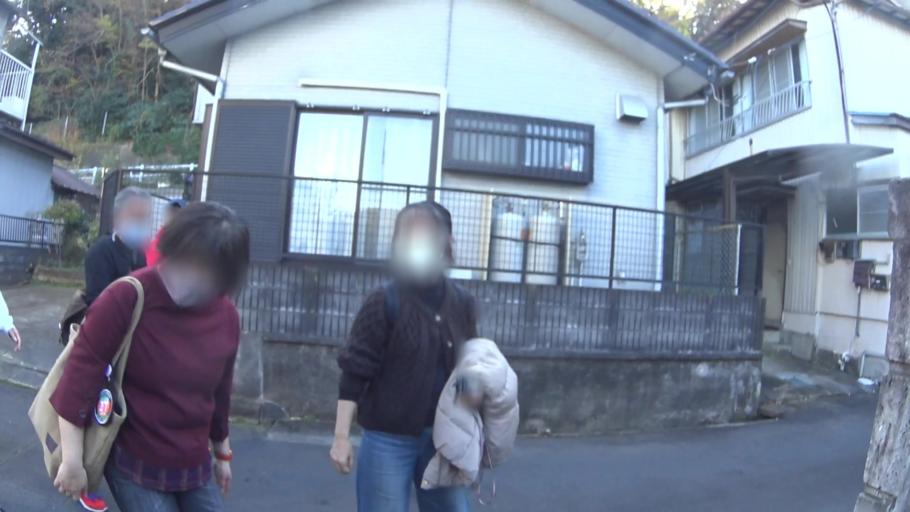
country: JP
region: Ibaraki
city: Mito-shi
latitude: 36.3820
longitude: 140.4711
